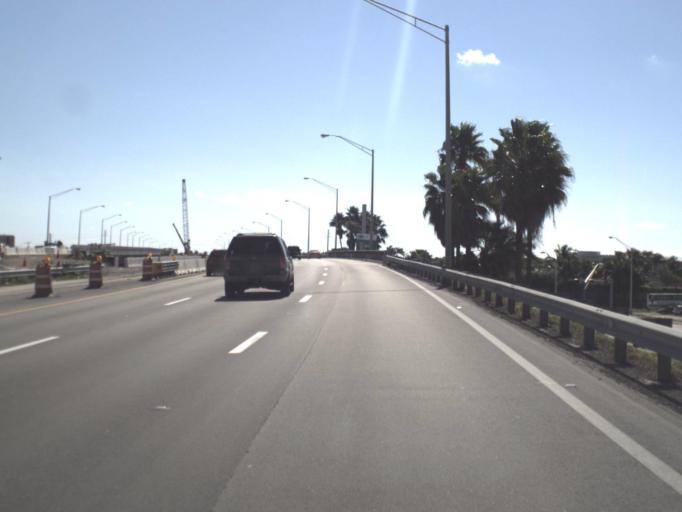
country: US
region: Florida
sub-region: Miami-Dade County
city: South Miami Heights
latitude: 25.5986
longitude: -80.3760
